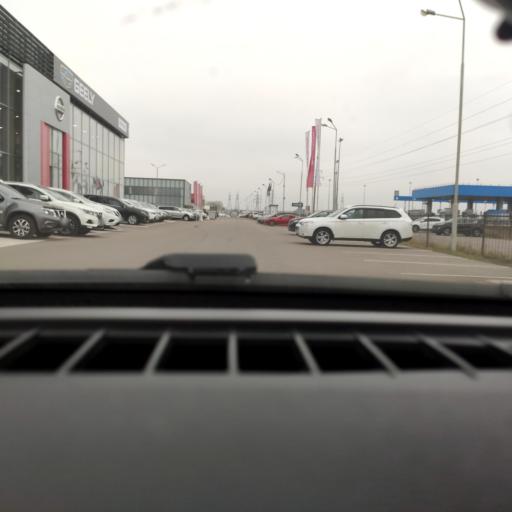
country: RU
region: Voronezj
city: Somovo
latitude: 51.6604
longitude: 39.3045
